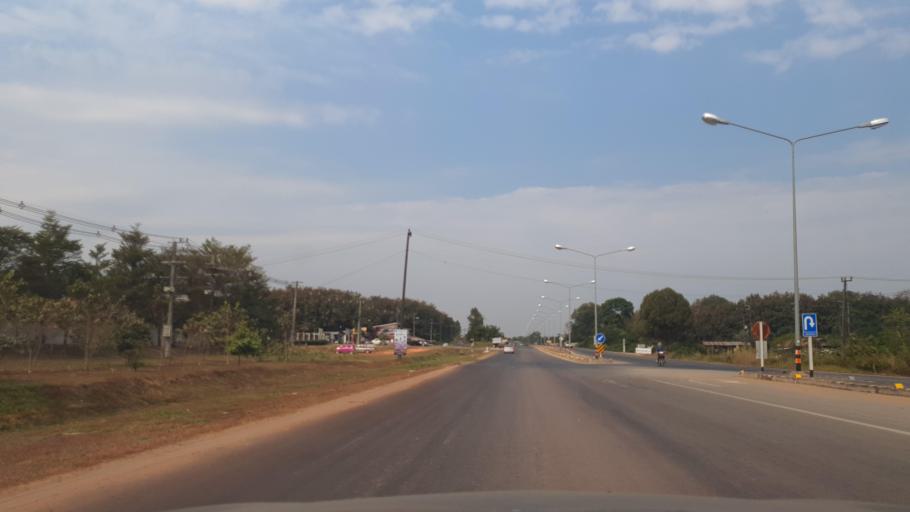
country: TH
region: Changwat Bueng Kan
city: Si Wilai
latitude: 18.2979
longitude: 103.8179
